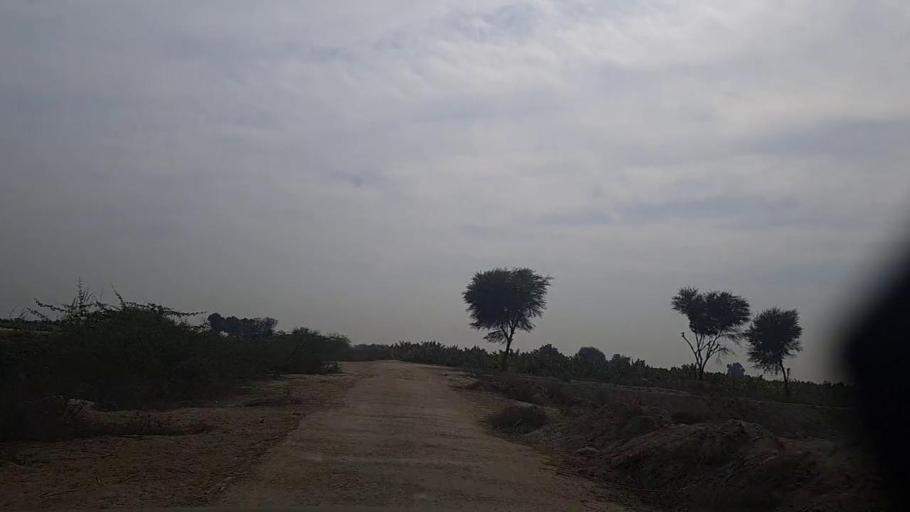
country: PK
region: Sindh
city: Sakrand
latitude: 26.2420
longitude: 68.2964
